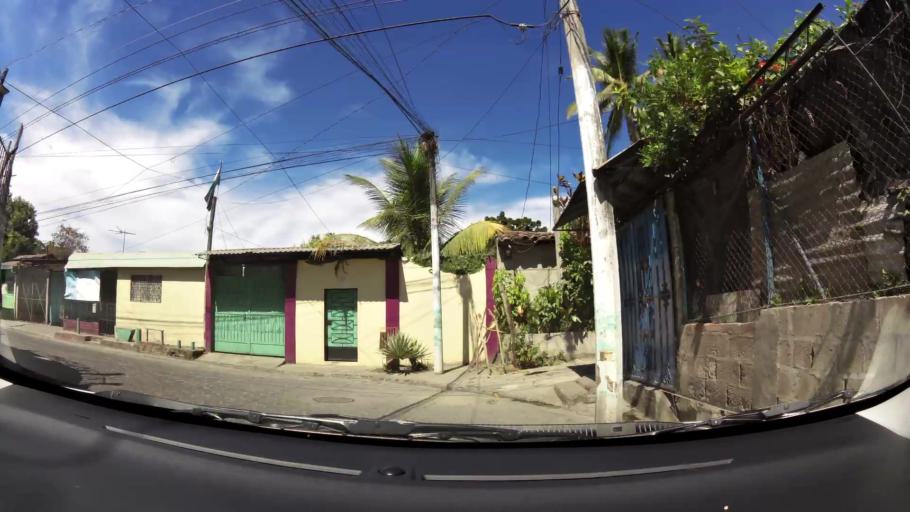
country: SV
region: San Salvador
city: Apopa
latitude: 13.8090
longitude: -89.1730
